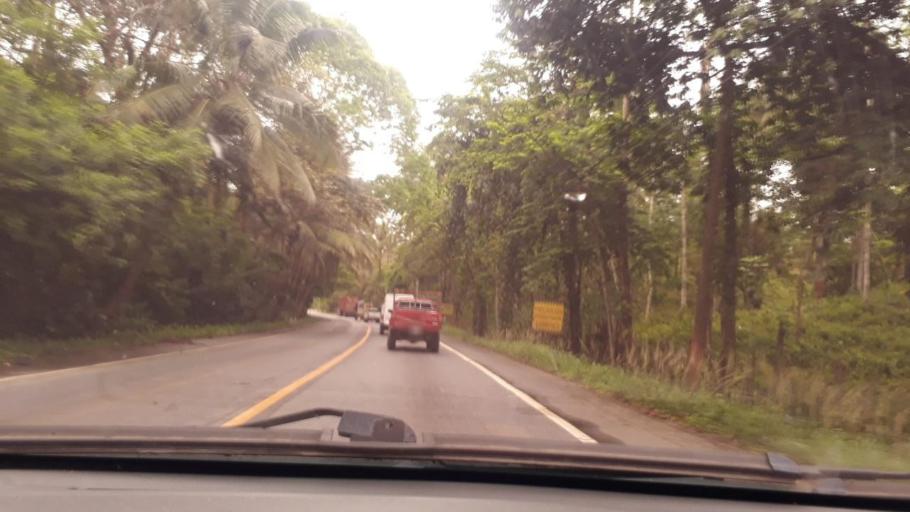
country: GT
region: Izabal
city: Morales
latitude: 15.5374
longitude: -88.7474
